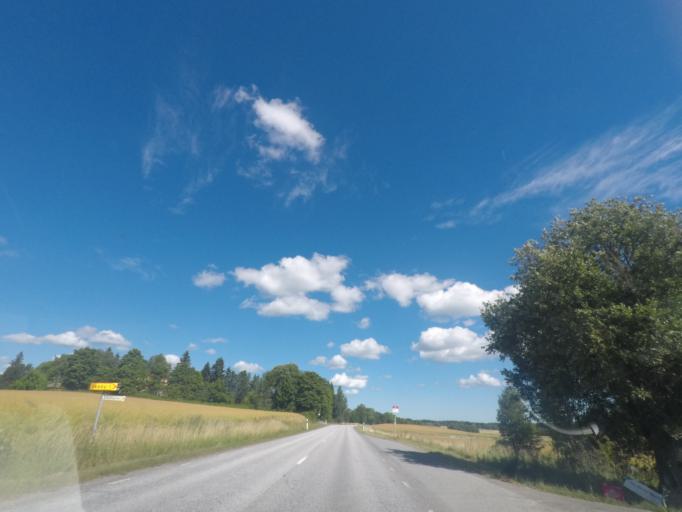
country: SE
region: Stockholm
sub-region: Norrtalje Kommun
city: Hallstavik
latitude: 59.9309
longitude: 18.7120
